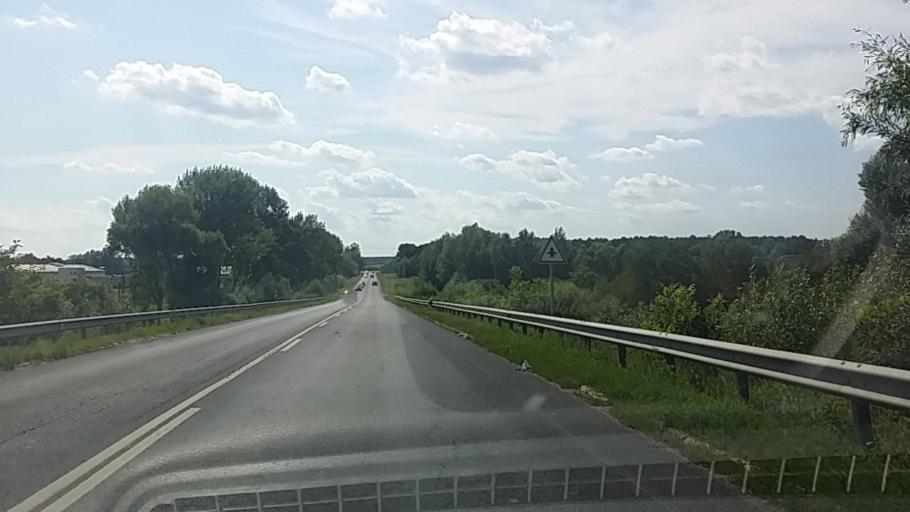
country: HU
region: Zala
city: Nagykanizsa
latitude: 46.4670
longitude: 16.9787
